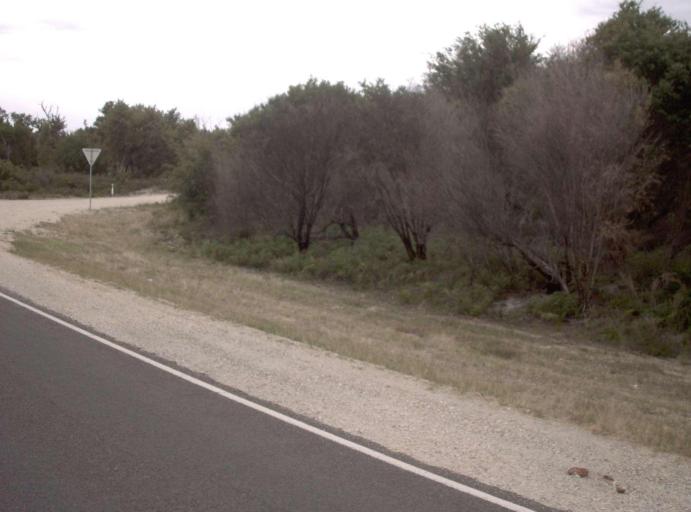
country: AU
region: Victoria
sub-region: East Gippsland
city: Bairnsdale
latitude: -38.0833
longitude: 147.5293
